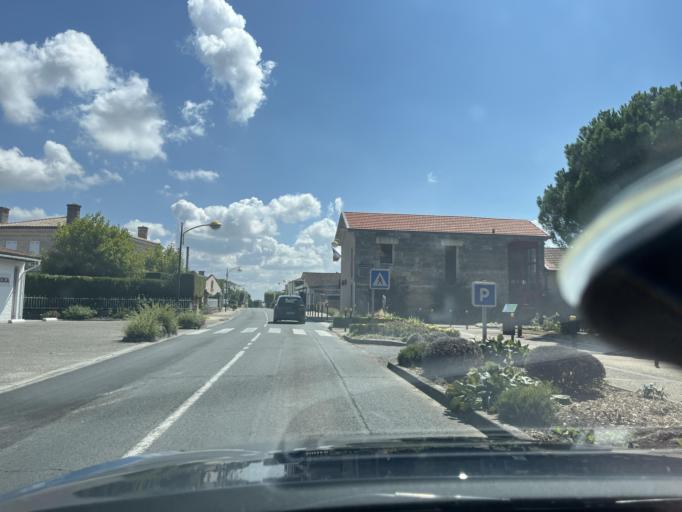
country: FR
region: Aquitaine
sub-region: Departement de la Gironde
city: Cantenac
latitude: 45.0643
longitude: -0.6179
